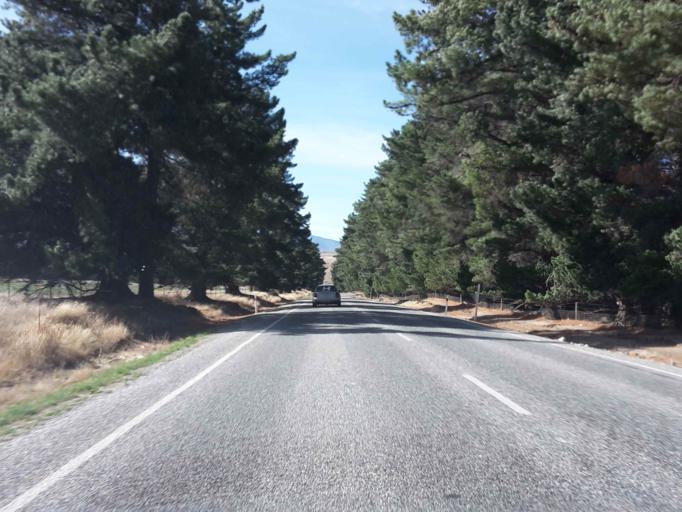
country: NZ
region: Otago
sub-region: Queenstown-Lakes District
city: Wanaka
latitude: -44.8067
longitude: 169.4530
